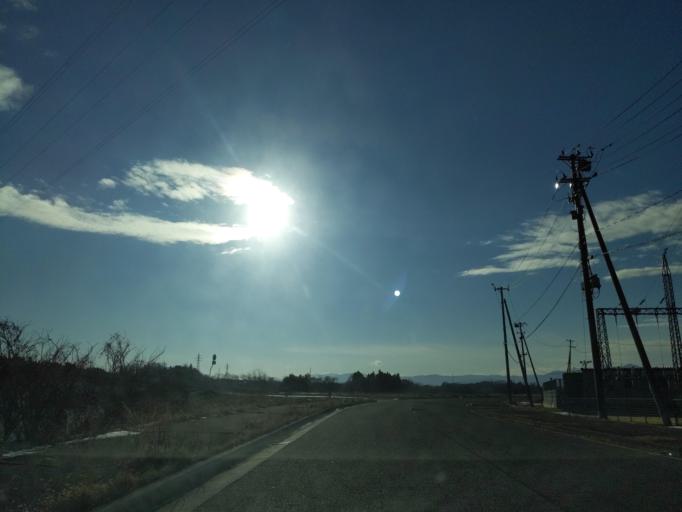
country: JP
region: Fukushima
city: Motomiya
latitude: 37.4744
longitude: 140.3722
